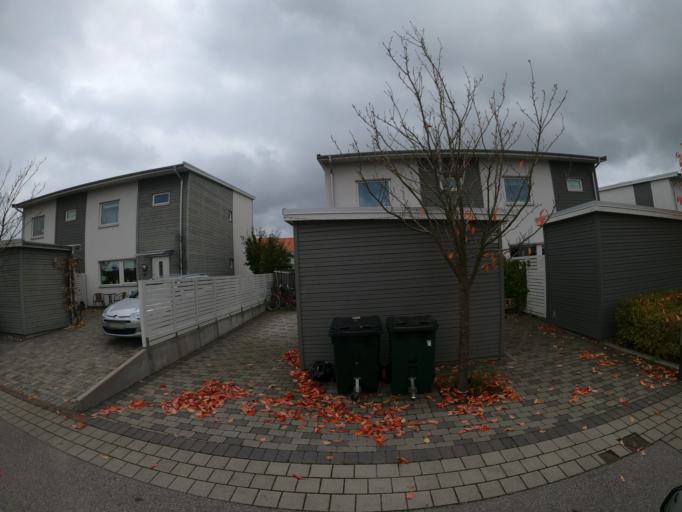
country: SE
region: Skane
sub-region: Lunds Kommun
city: Genarp
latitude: 55.6597
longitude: 13.3602
